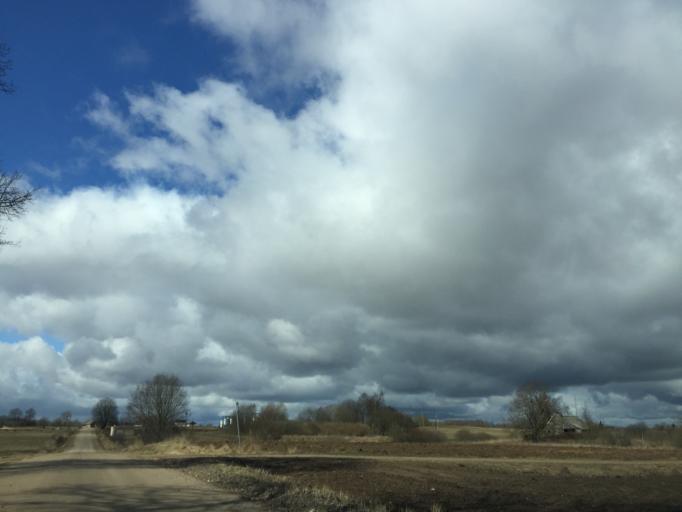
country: LV
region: Akniste
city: Akniste
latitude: 56.1004
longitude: 25.9721
